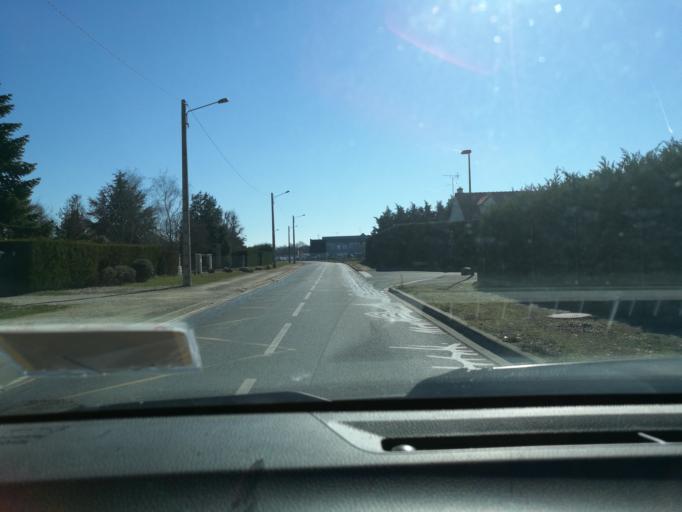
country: FR
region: Centre
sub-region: Departement du Loiret
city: Saint-Jean-le-Blanc
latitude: 47.8733
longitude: 1.9268
